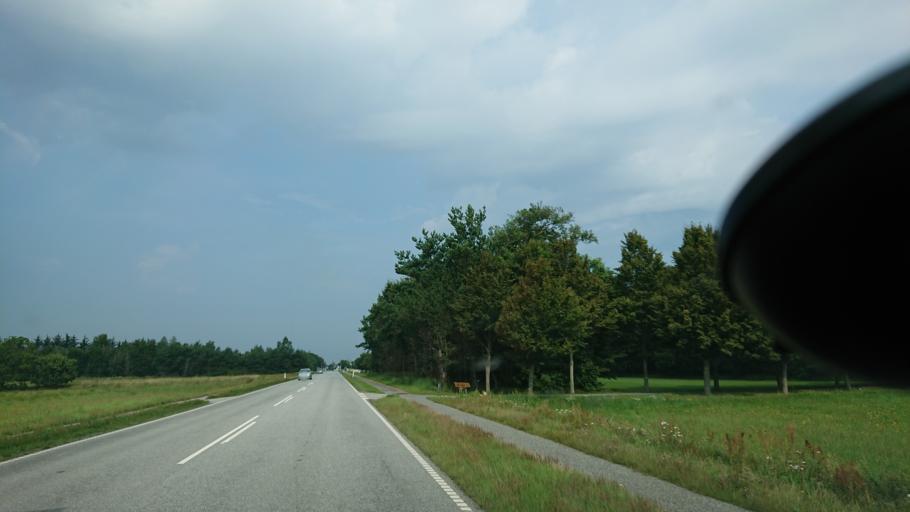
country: DK
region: North Denmark
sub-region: Frederikshavn Kommune
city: Strandby
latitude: 57.5270
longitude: 10.4238
